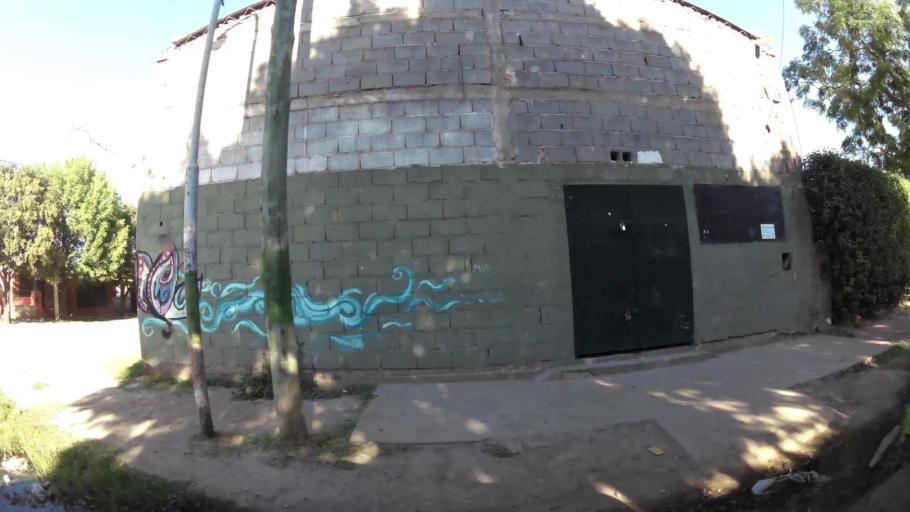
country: AR
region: Cordoba
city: Villa Allende
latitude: -31.3327
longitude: -64.2410
